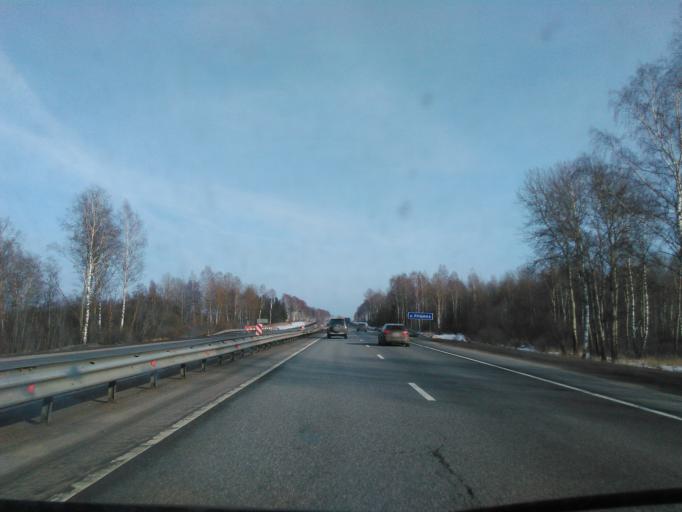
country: RU
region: Smolensk
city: Verkhnedneprovskiy
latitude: 55.1815
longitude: 33.5879
